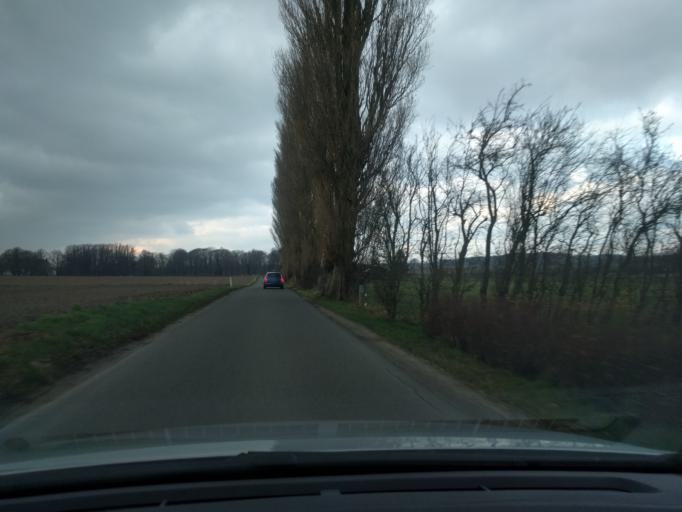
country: DK
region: South Denmark
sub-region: Nyborg Kommune
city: Ullerslev
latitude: 55.3887
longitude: 10.6382
